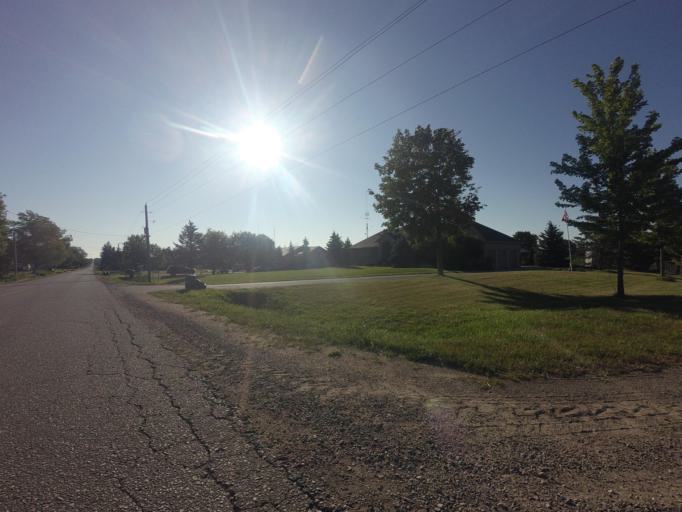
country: CA
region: Ontario
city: Bradford West Gwillimbury
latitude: 44.0550
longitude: -79.7148
